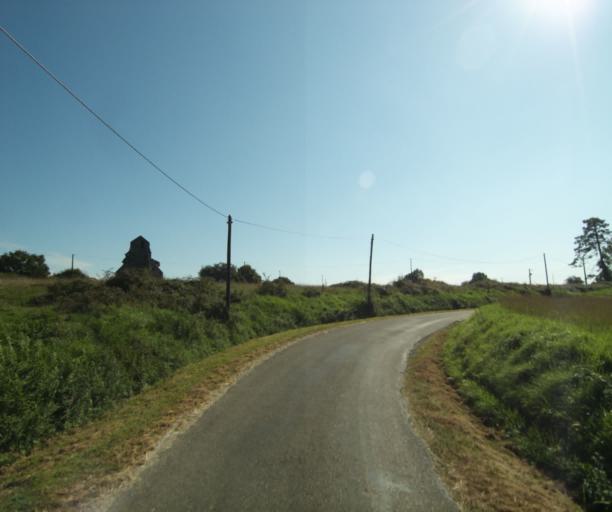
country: FR
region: Aquitaine
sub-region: Departement des Landes
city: Gabarret
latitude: 43.9443
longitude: -0.0127
